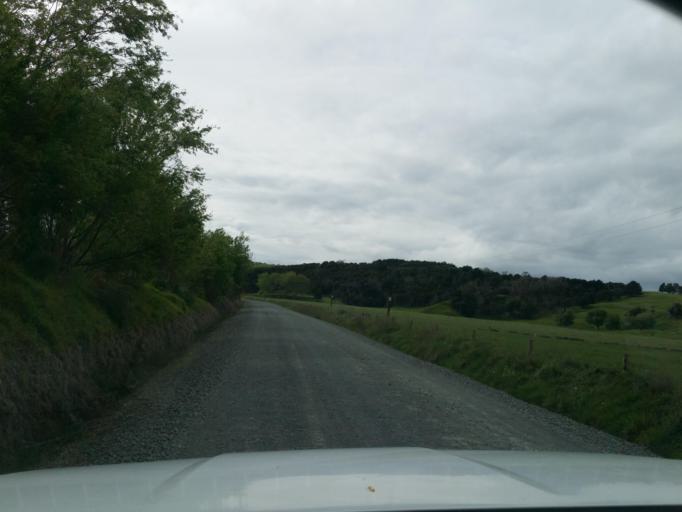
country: NZ
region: Northland
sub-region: Kaipara District
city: Dargaville
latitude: -35.9034
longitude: 173.9218
